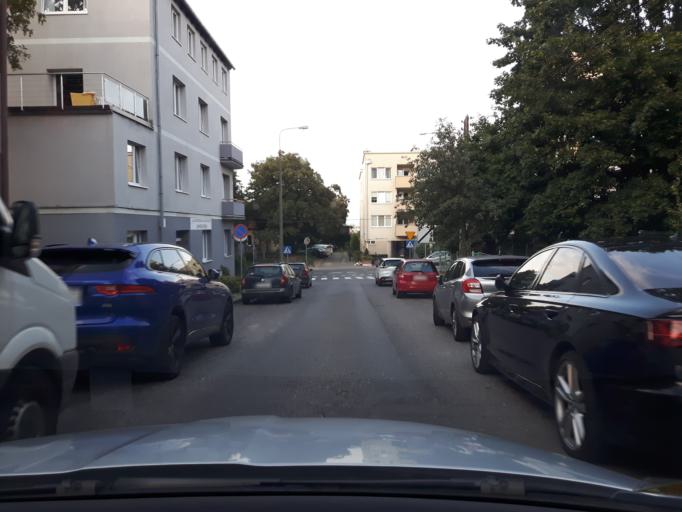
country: PL
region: Pomeranian Voivodeship
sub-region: Gdynia
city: Gdynia
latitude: 54.5181
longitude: 18.5285
